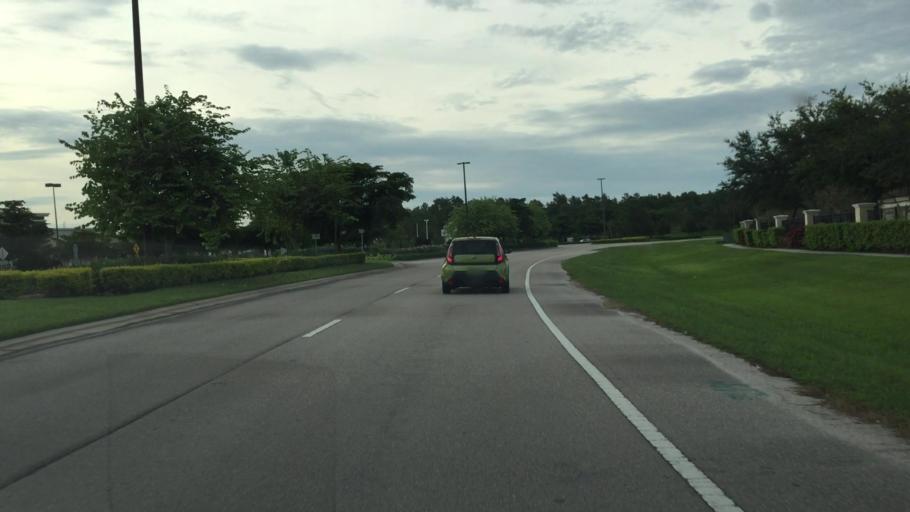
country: US
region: Florida
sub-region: Lee County
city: Fort Myers
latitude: 26.6166
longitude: -81.7970
